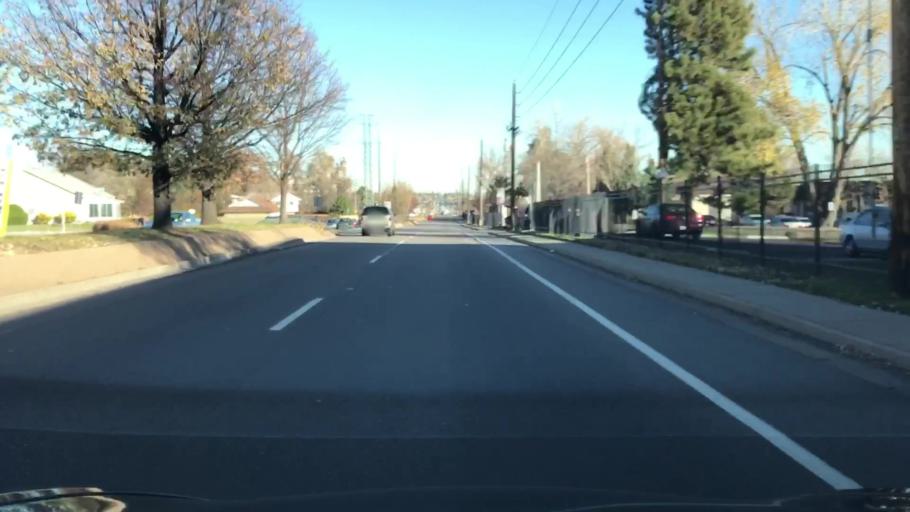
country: US
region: Colorado
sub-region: Arapahoe County
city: Glendale
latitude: 39.6720
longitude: -104.9035
